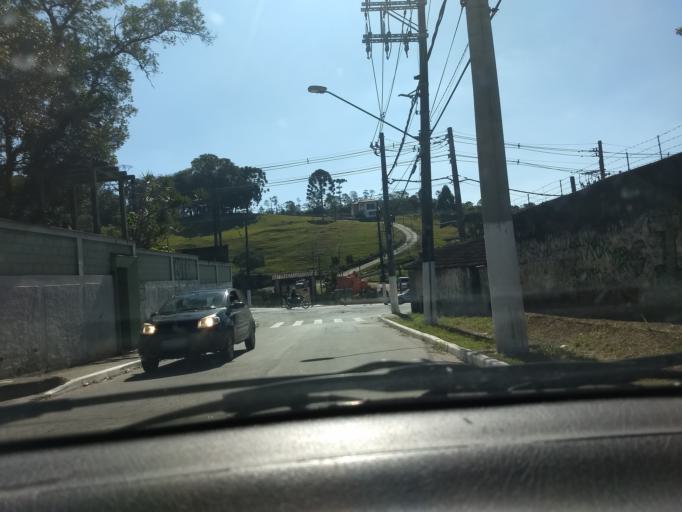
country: BR
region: Sao Paulo
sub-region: Embu-Guacu
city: Embu Guacu
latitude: -23.8388
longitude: -46.7329
